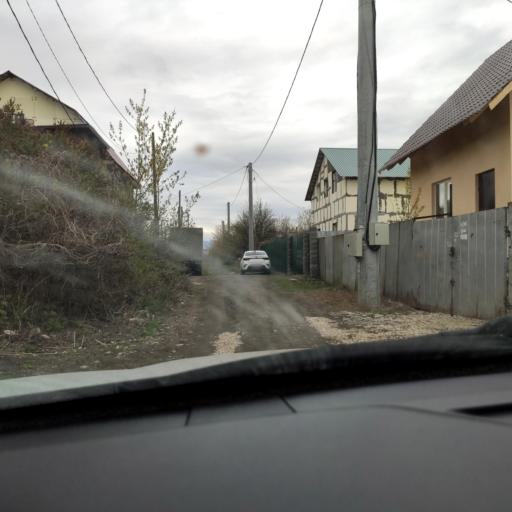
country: RU
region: Samara
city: Petra-Dubrava
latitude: 53.2601
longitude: 50.3437
